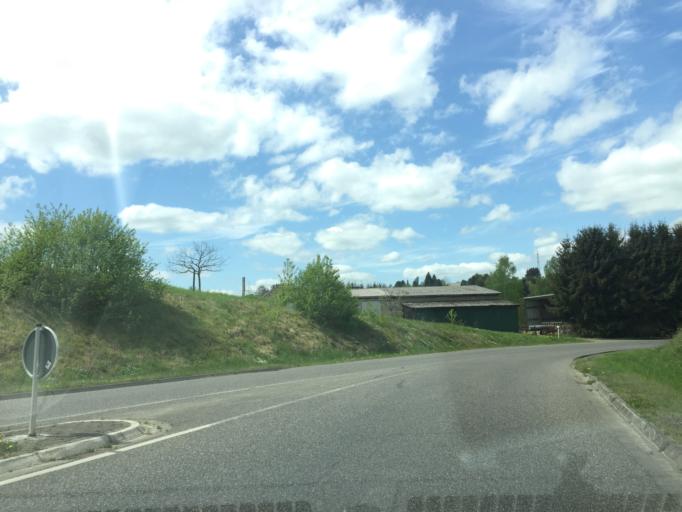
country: DE
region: Rheinland-Pfalz
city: Meudt
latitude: 50.4900
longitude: 7.8993
